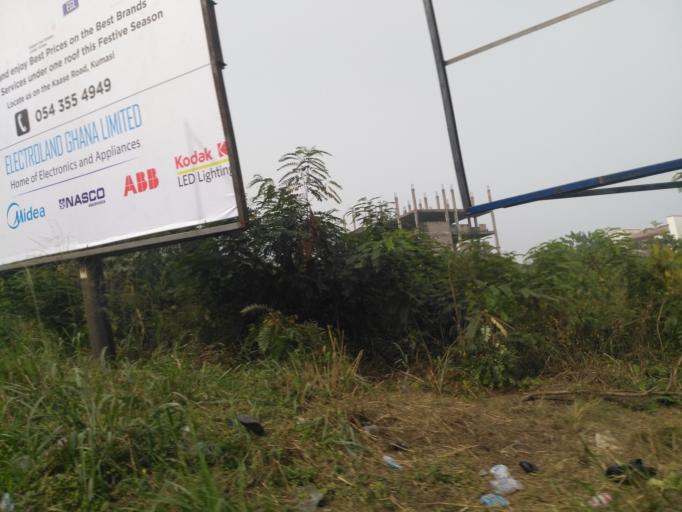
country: GH
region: Ashanti
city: Kumasi
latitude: 6.6872
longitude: -1.6278
